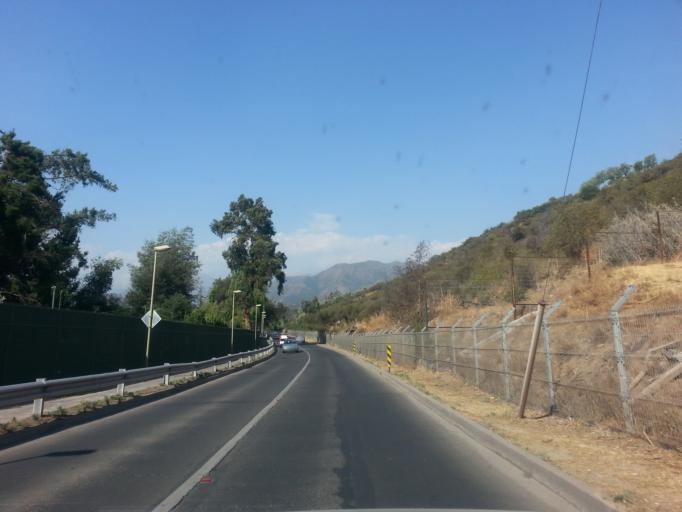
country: CL
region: Santiago Metropolitan
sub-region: Provincia de Santiago
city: Villa Presidente Frei, Nunoa, Santiago, Chile
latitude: -33.3849
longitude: -70.5183
